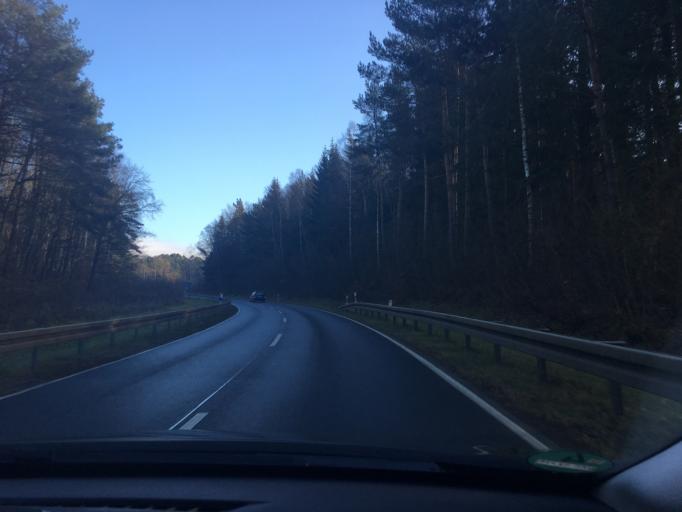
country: DE
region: Hesse
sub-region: Regierungsbezirk Kassel
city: Dipperz
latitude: 50.5707
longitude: 9.7712
